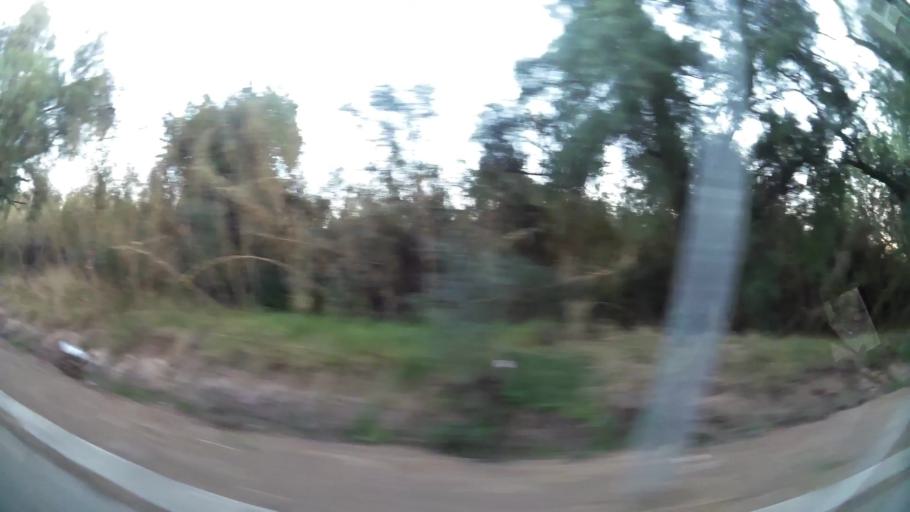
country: ZA
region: Northern Cape
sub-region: Frances Baard District Municipality
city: Kimberley
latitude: -28.7222
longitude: 24.7742
